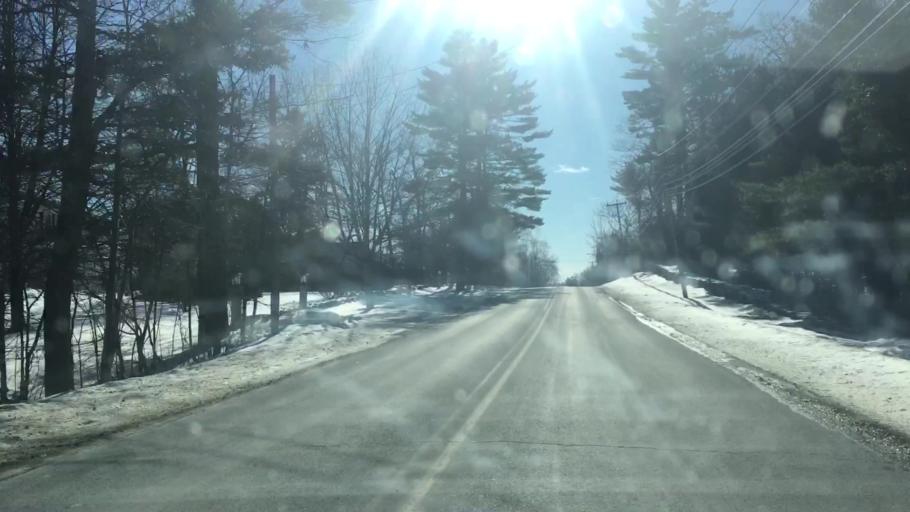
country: US
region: Maine
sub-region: Hancock County
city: Ellsworth
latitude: 44.5357
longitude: -68.4309
